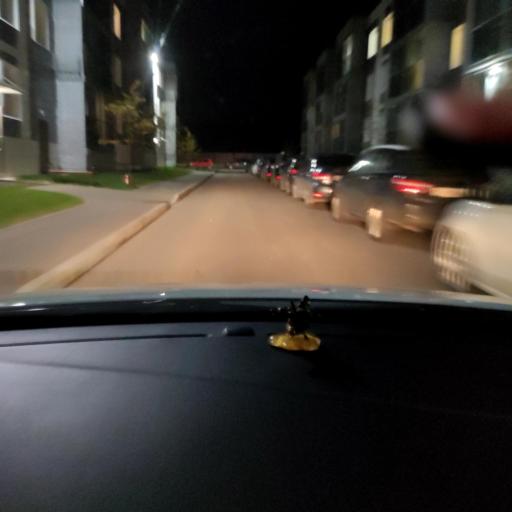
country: RU
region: Tatarstan
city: Vysokaya Gora
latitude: 55.8093
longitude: 49.4326
